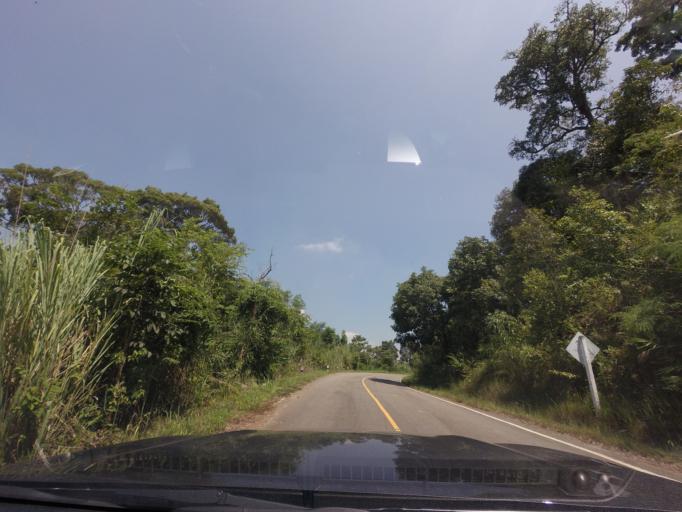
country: TH
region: Loei
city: Na Haeo
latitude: 17.5727
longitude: 100.8968
